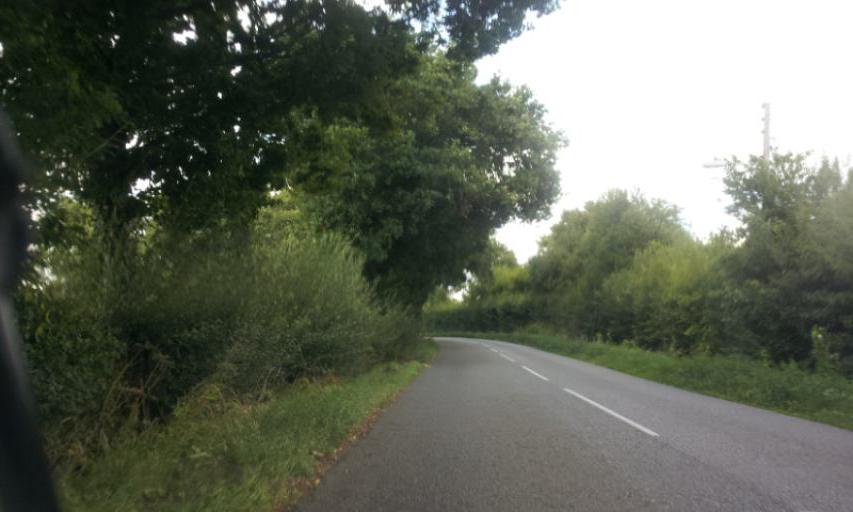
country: GB
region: England
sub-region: Kent
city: Staplehurst
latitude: 51.1746
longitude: 0.5789
